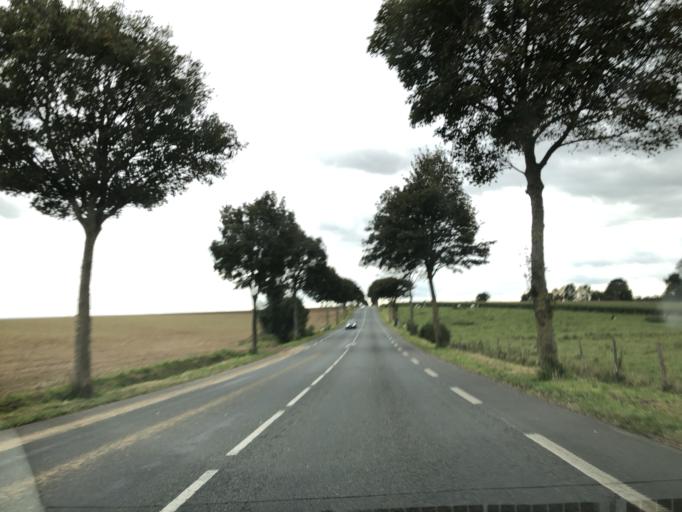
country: FR
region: Nord-Pas-de-Calais
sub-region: Departement du Pas-de-Calais
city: Fruges
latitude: 50.4688
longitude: 2.1065
